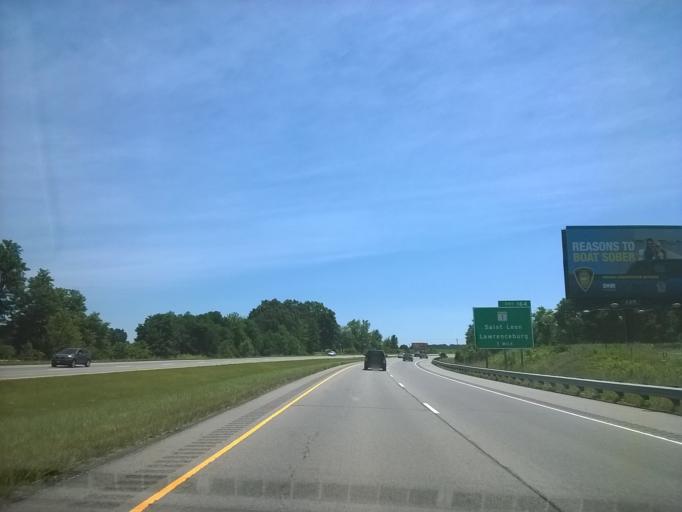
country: US
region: Indiana
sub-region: Ripley County
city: Sunman
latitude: 39.2881
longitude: -84.9806
